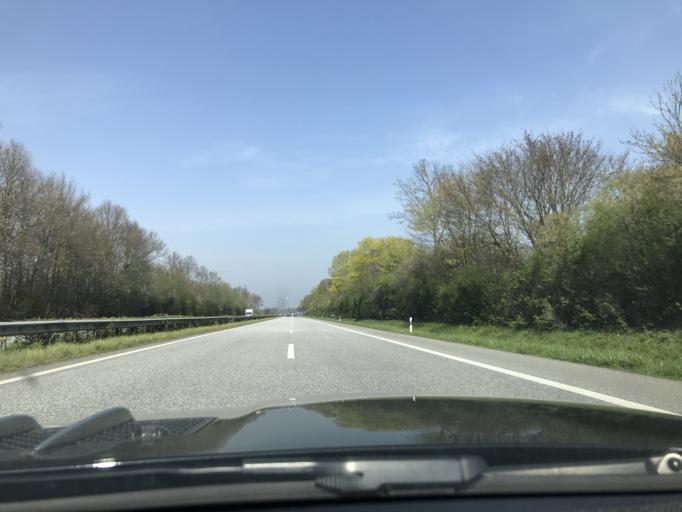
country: DE
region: Schleswig-Holstein
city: Manhagen
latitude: 54.1979
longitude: 10.8979
